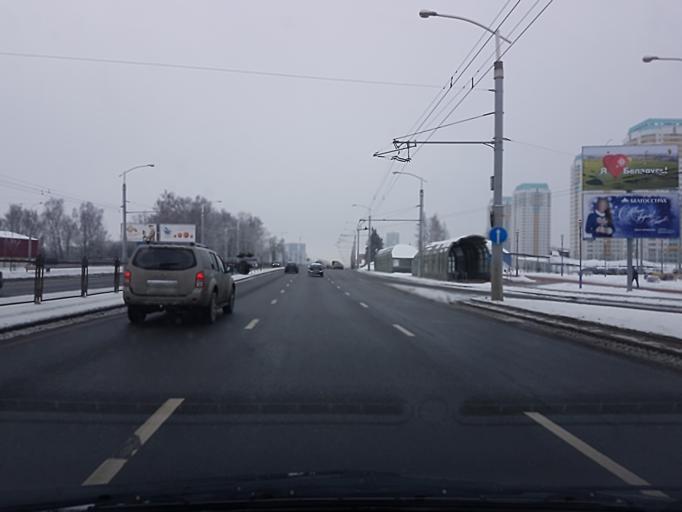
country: BY
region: Minsk
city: Novoye Medvezhino
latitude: 53.8693
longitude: 27.4912
